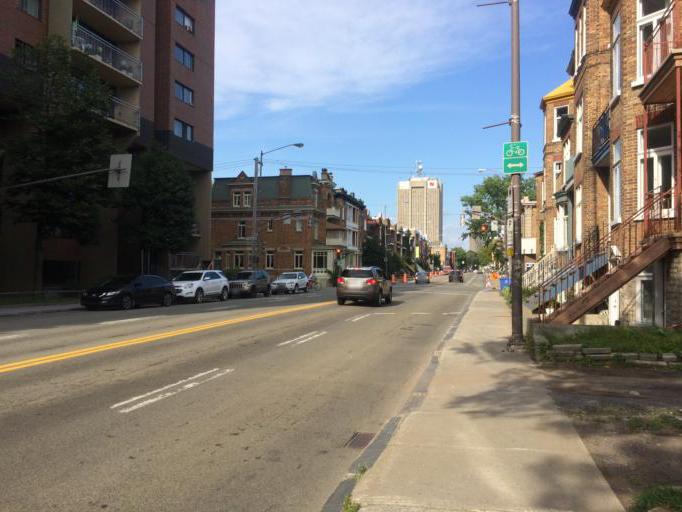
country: CA
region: Quebec
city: Quebec
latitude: 46.8029
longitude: -71.2290
